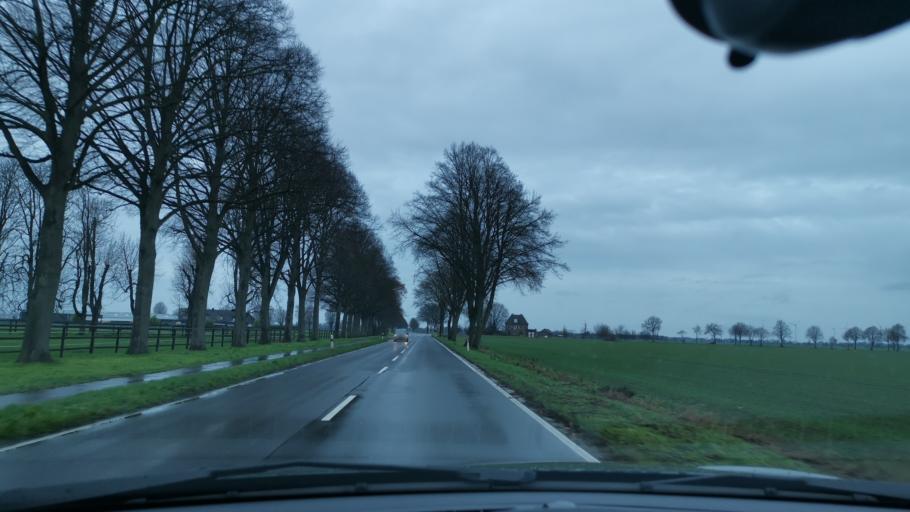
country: DE
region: North Rhine-Westphalia
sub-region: Regierungsbezirk Koln
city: Bedburg
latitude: 50.9874
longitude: 6.5100
